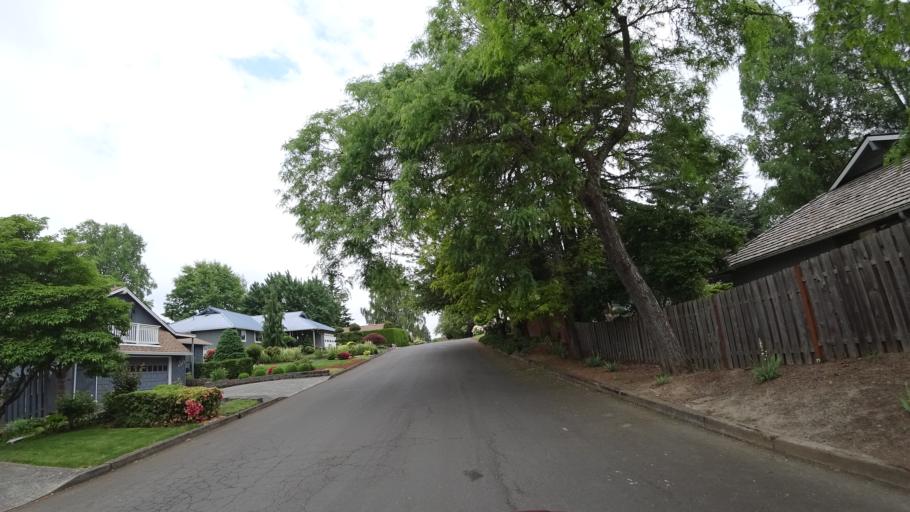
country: US
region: Oregon
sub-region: Clackamas County
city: Milwaukie
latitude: 45.4866
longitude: -122.6324
